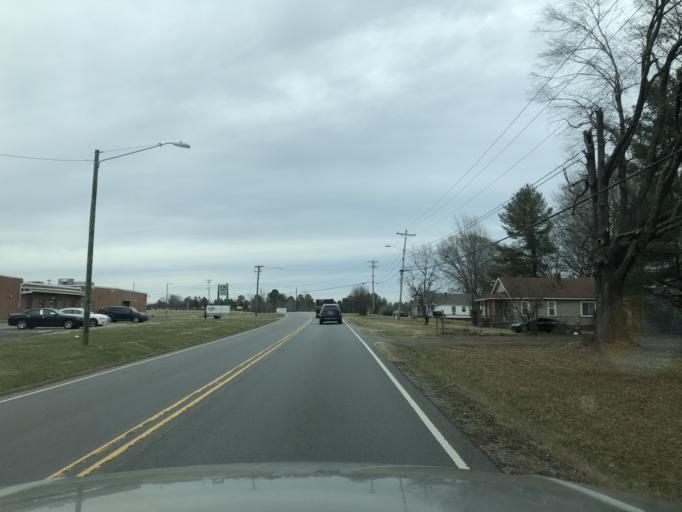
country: US
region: North Carolina
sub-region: Cleveland County
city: Shelby
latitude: 35.2967
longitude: -81.4865
